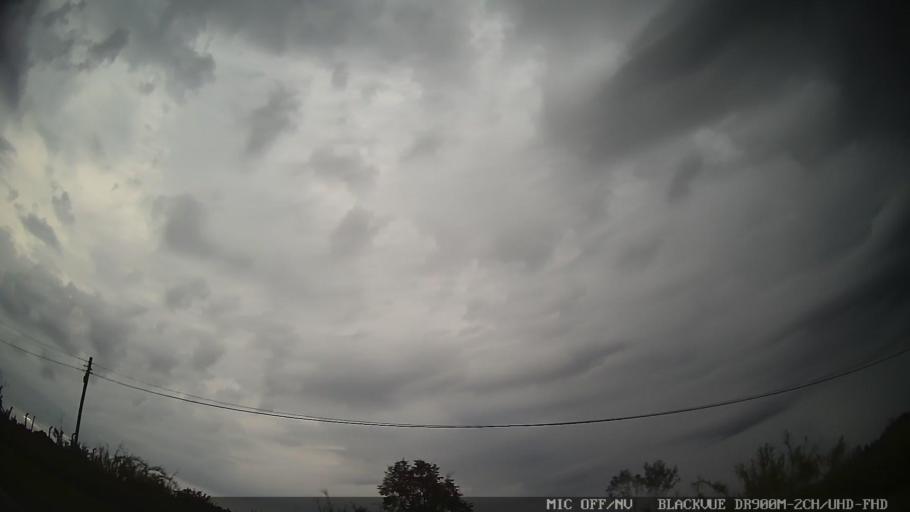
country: BR
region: Sao Paulo
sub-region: Amparo
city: Amparo
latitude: -22.7433
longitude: -46.7615
